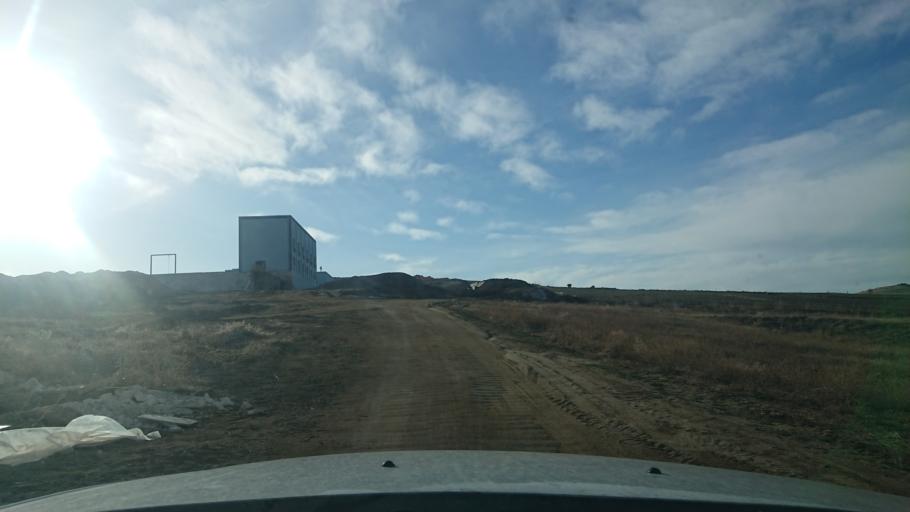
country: TR
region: Aksaray
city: Agacoren
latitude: 38.8474
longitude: 33.9432
